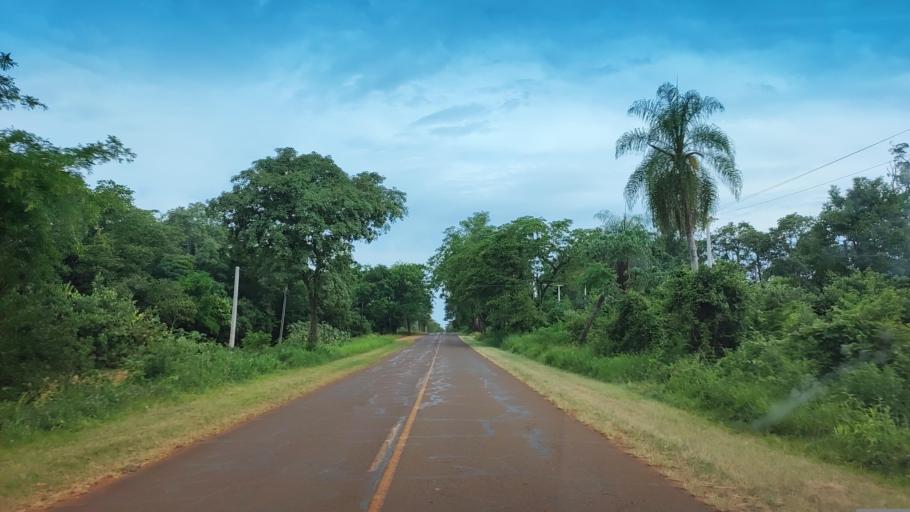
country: AR
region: Misiones
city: Gobernador Roca
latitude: -27.1430
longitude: -55.4958
